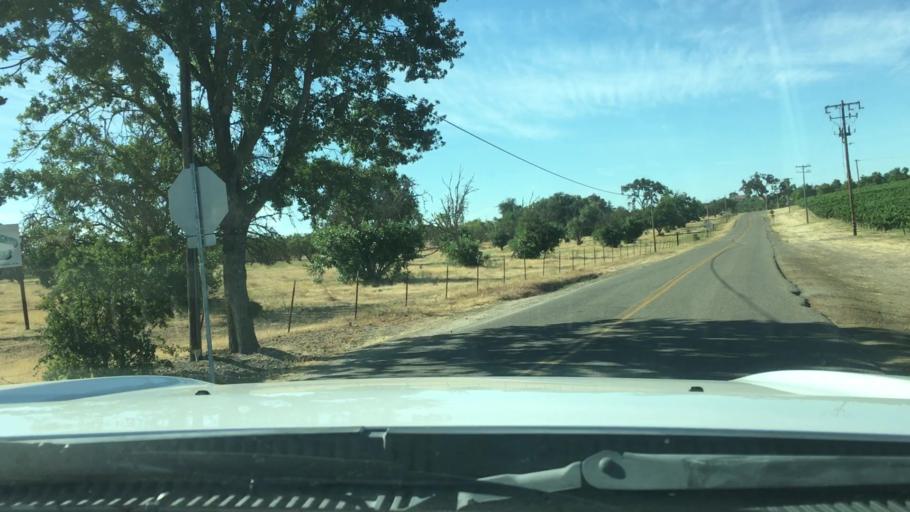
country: US
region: California
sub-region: San Luis Obispo County
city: Atascadero
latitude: 35.5527
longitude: -120.6114
